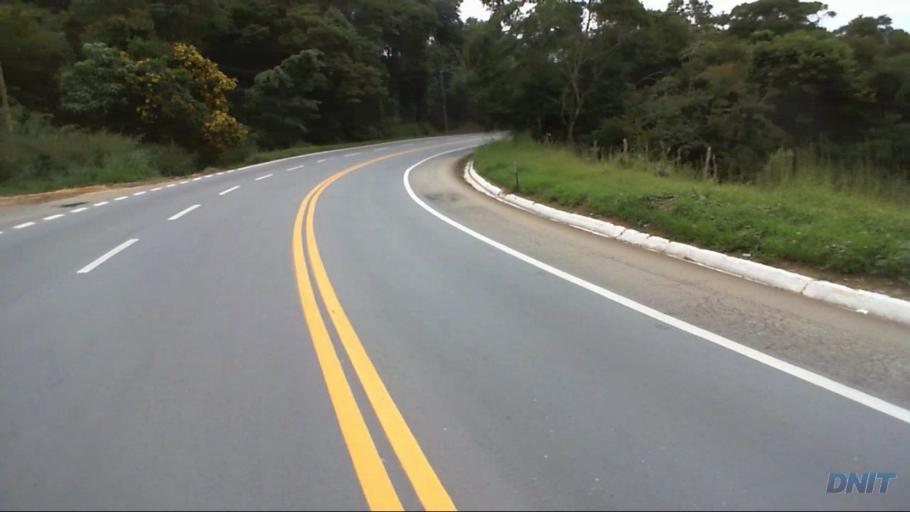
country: BR
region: Minas Gerais
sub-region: Caete
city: Caete
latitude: -19.7430
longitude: -43.5210
